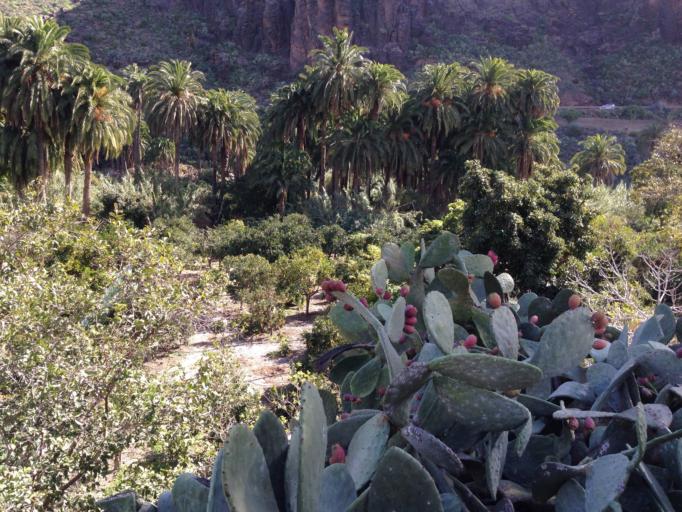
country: ES
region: Canary Islands
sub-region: Provincia de Las Palmas
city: Santa Lucia
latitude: 27.8462
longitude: -15.5689
